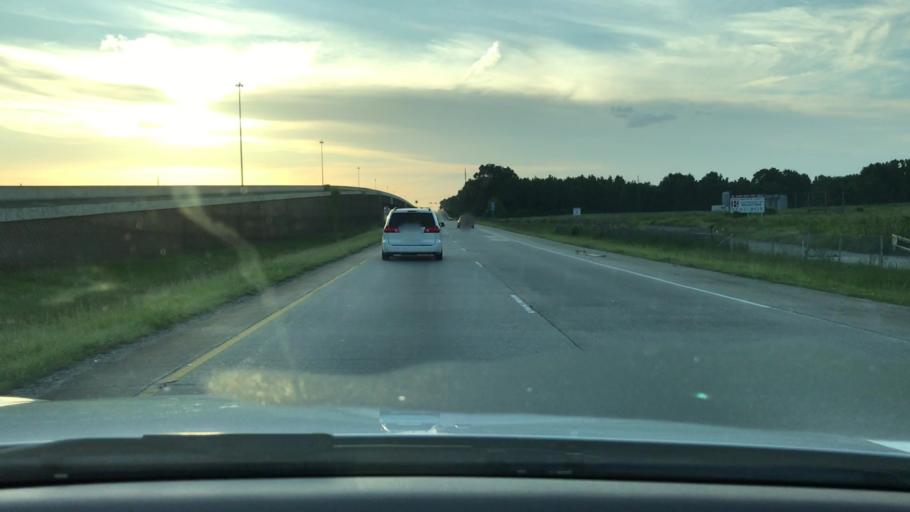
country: US
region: Louisiana
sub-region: East Baton Rouge Parish
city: Village Saint George
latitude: 30.3853
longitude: -91.0697
